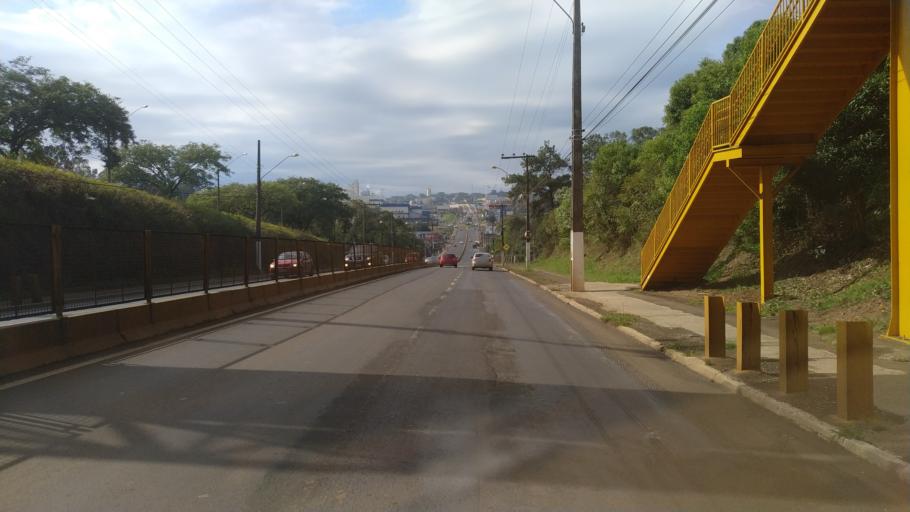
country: BR
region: Santa Catarina
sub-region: Chapeco
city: Chapeco
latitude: -27.0973
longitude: -52.6593
